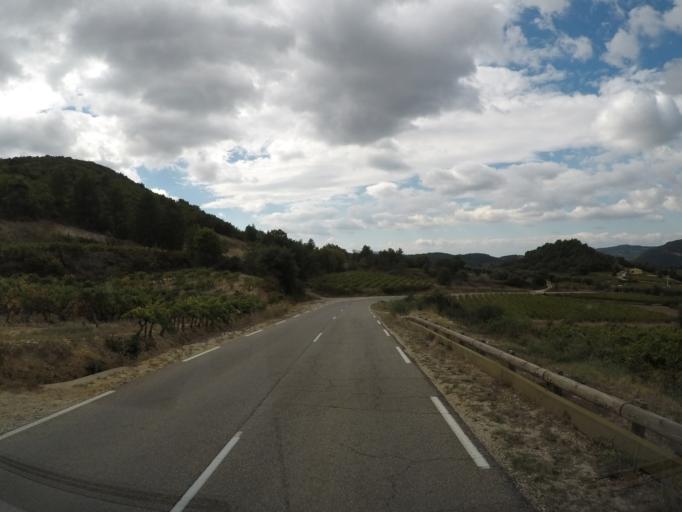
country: FR
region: Provence-Alpes-Cote d'Azur
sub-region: Departement du Vaucluse
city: Malaucene
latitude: 44.2294
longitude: 5.1811
